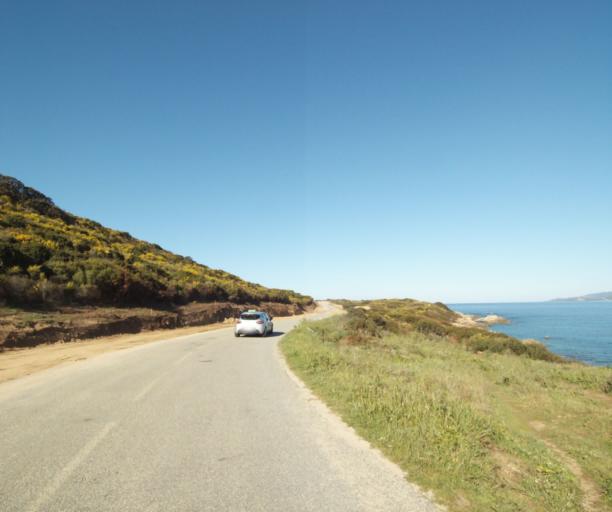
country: FR
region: Corsica
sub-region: Departement de la Corse-du-Sud
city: Propriano
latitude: 41.6709
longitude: 8.8878
